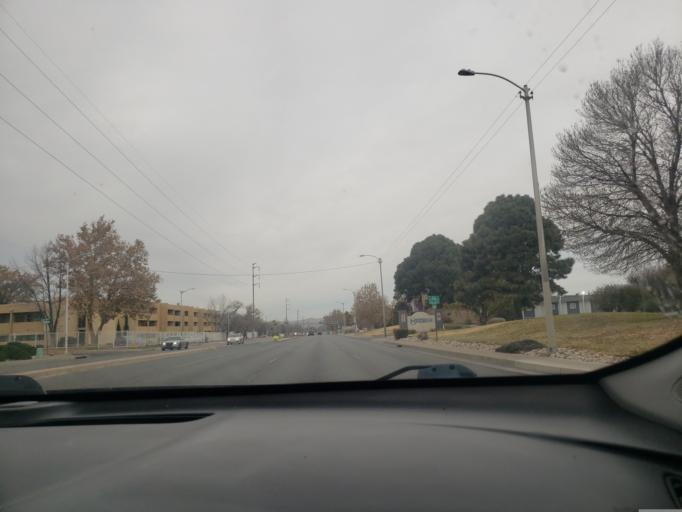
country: US
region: New Mexico
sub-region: Bernalillo County
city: North Valley
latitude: 35.1310
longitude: -106.5946
